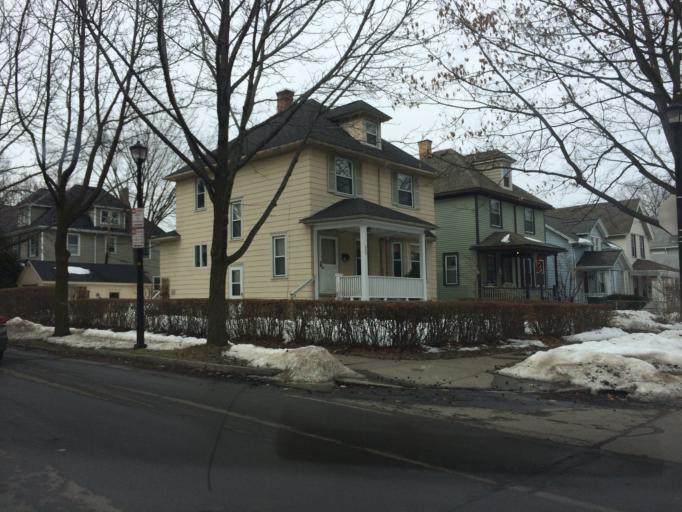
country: US
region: New York
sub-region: Monroe County
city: Rochester
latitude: 43.1380
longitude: -77.6035
